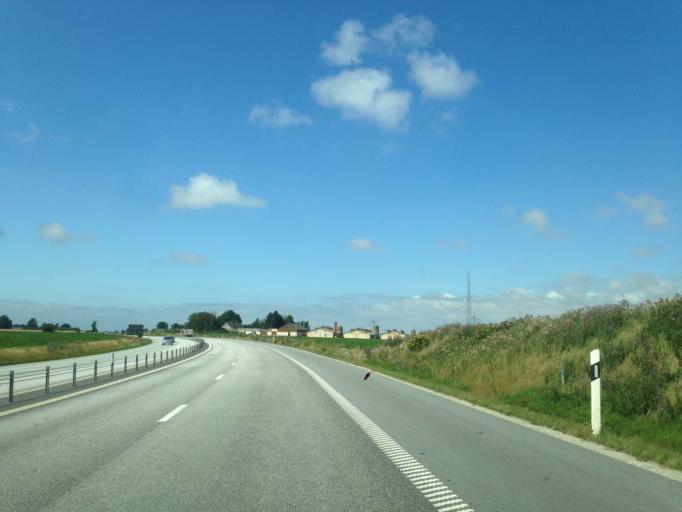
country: SE
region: Skane
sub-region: Trelleborgs Kommun
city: Skare
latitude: 55.4204
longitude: 13.0614
